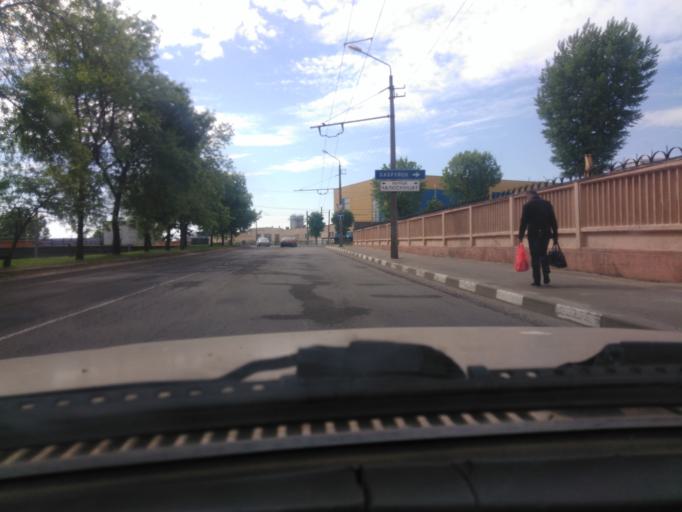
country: BY
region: Mogilev
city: Buynichy
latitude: 53.8927
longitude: 30.2987
